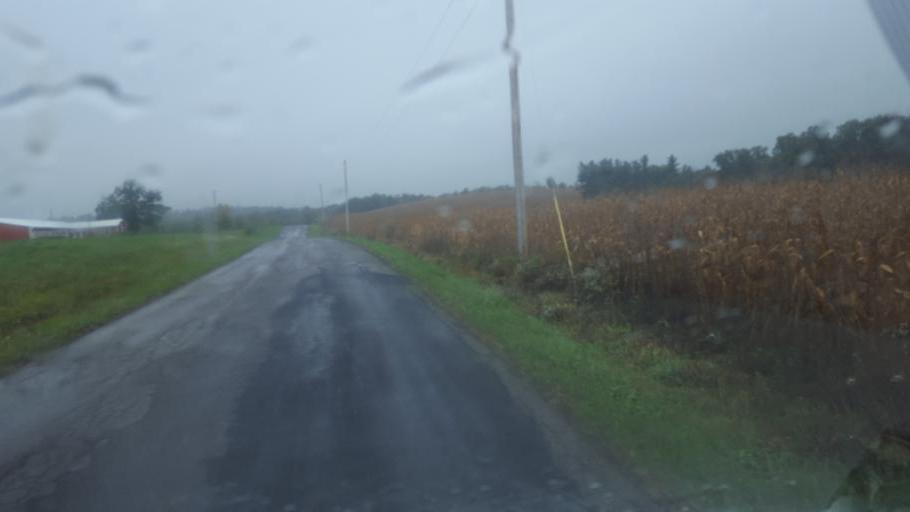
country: US
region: Ohio
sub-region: Knox County
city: Danville
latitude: 40.5025
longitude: -82.3224
